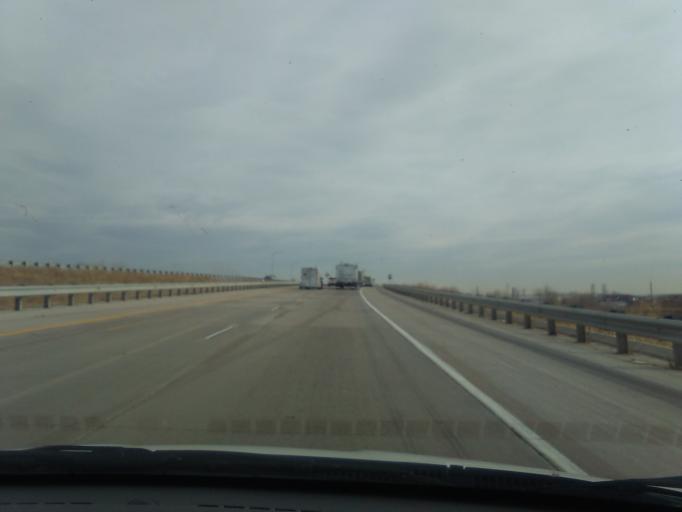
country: US
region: Colorado
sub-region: Adams County
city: Derby
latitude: 39.8800
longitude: -104.8867
